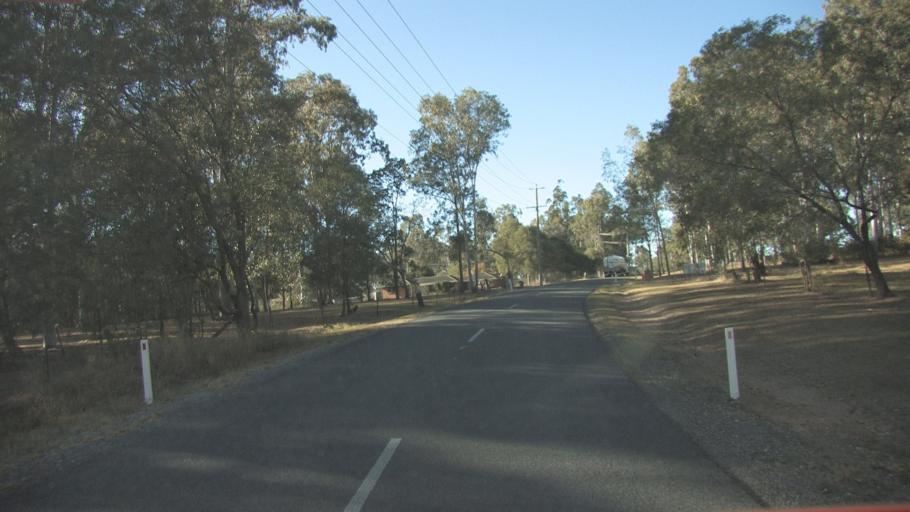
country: AU
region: Queensland
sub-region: Logan
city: North Maclean
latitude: -27.7967
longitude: 152.9917
